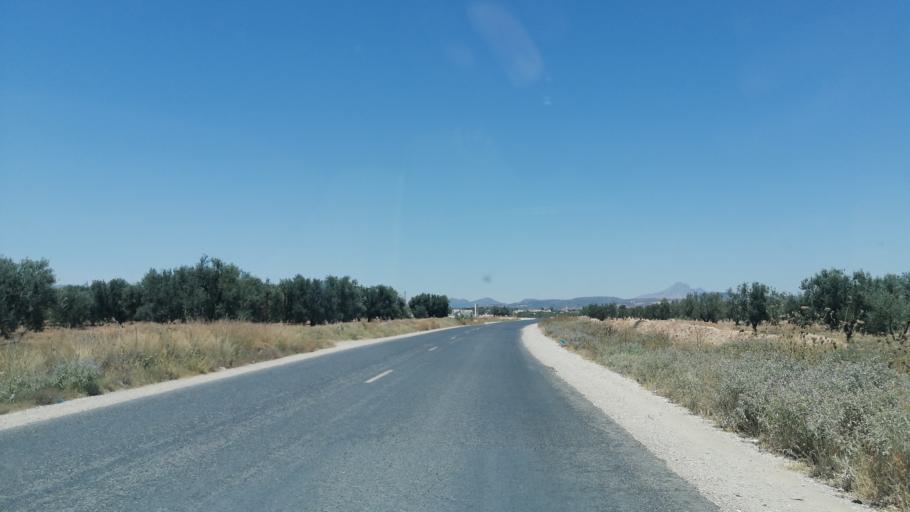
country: TN
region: Al Qayrawan
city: Sbikha
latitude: 36.1327
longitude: 10.0915
